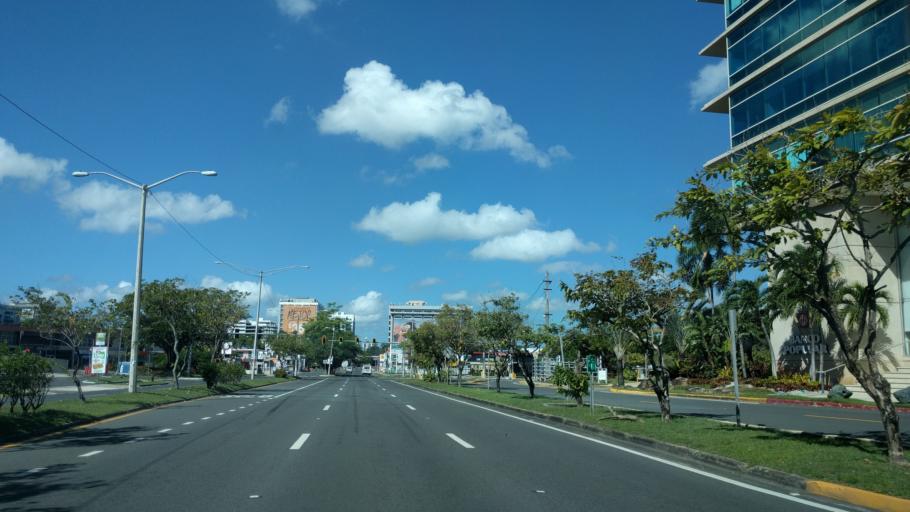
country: PR
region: Catano
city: Catano
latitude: 18.4132
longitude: -66.0968
